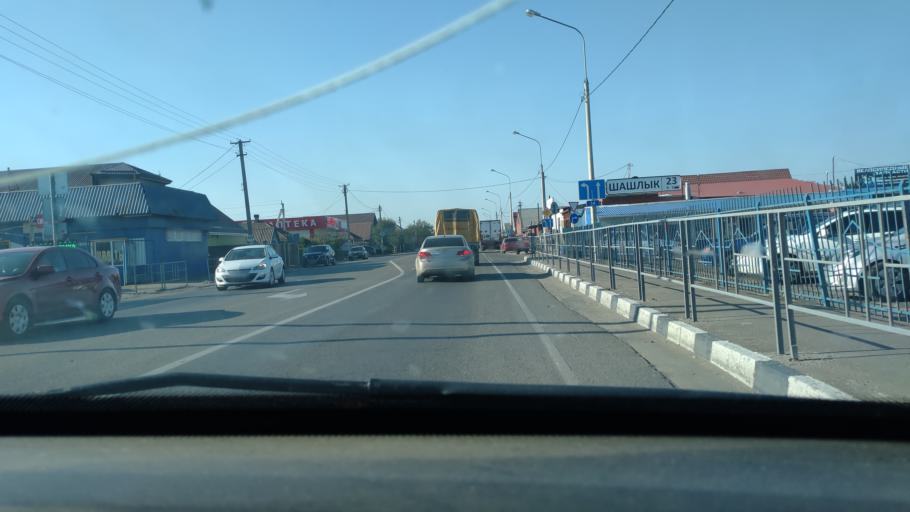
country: RU
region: Krasnodarskiy
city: Novotitarovskaya
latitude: 45.2451
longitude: 38.9975
